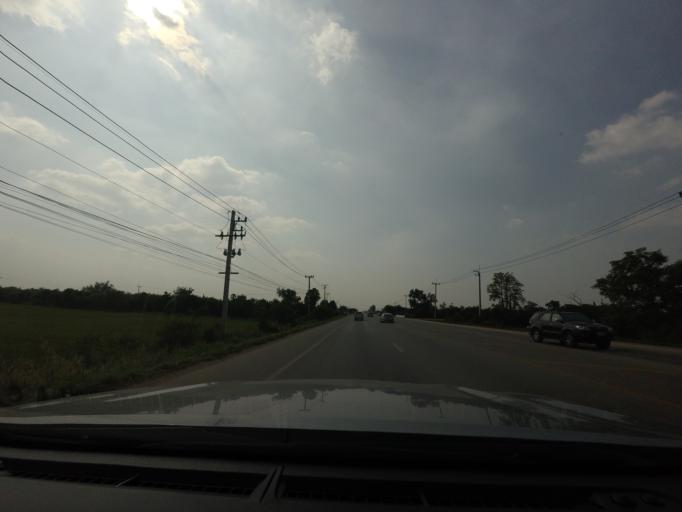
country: TH
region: Phitsanulok
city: Bang Rakam
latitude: 16.7694
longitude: 100.1542
